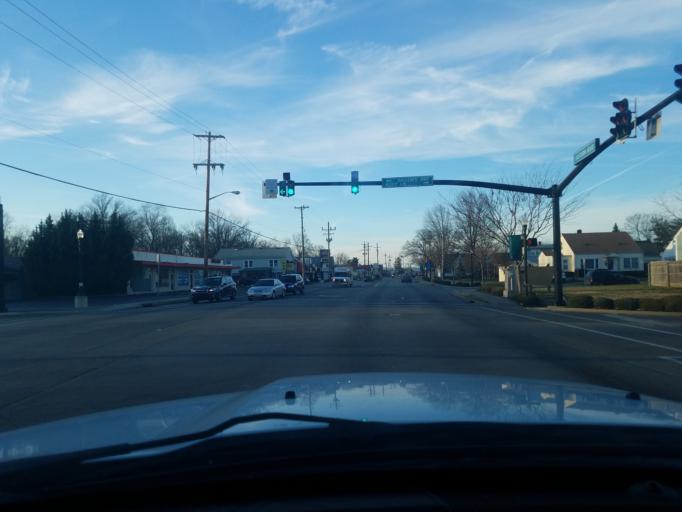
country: US
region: Indiana
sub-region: Clark County
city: Clarksville
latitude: 38.2967
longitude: -85.7597
